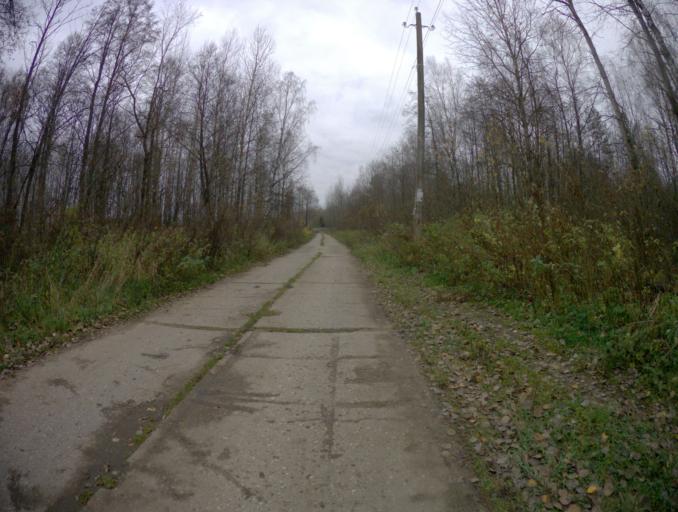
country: RU
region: Moskovskaya
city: Malaya Dubna
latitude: 55.9887
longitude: 38.9581
